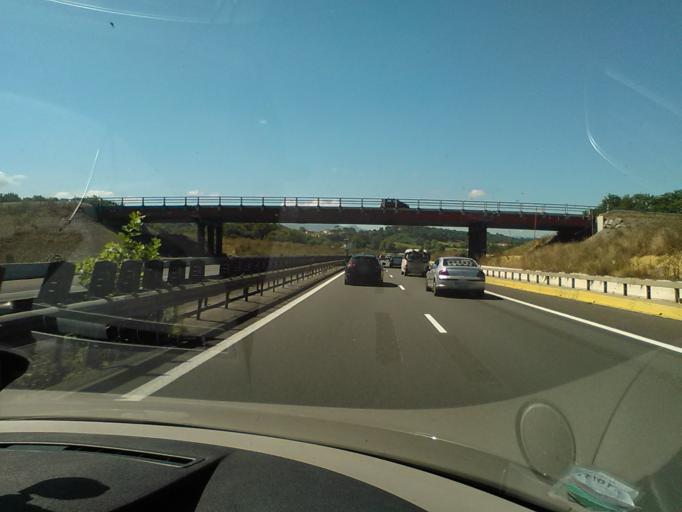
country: FR
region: Aquitaine
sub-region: Departement des Pyrenees-Atlantiques
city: Bidart
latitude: 43.4371
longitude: -1.5715
